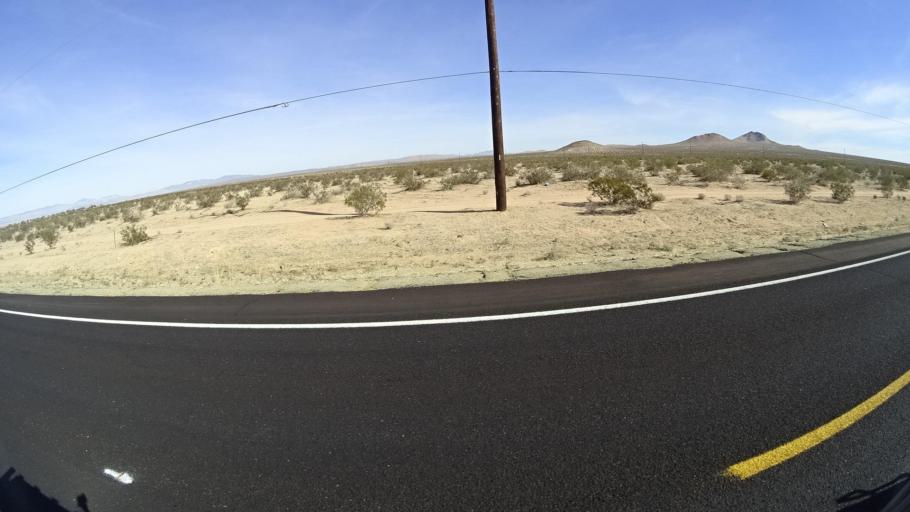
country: US
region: California
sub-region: Kern County
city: California City
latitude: 35.1100
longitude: -117.9276
